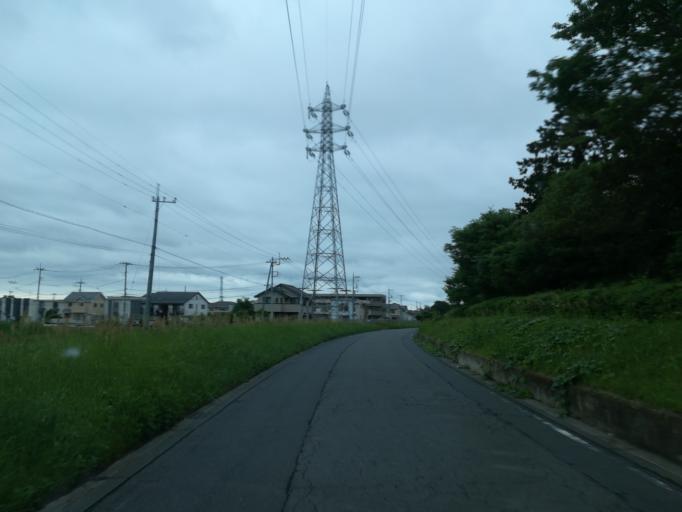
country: JP
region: Ibaraki
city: Tsukuba
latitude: 36.1225
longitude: 140.0893
